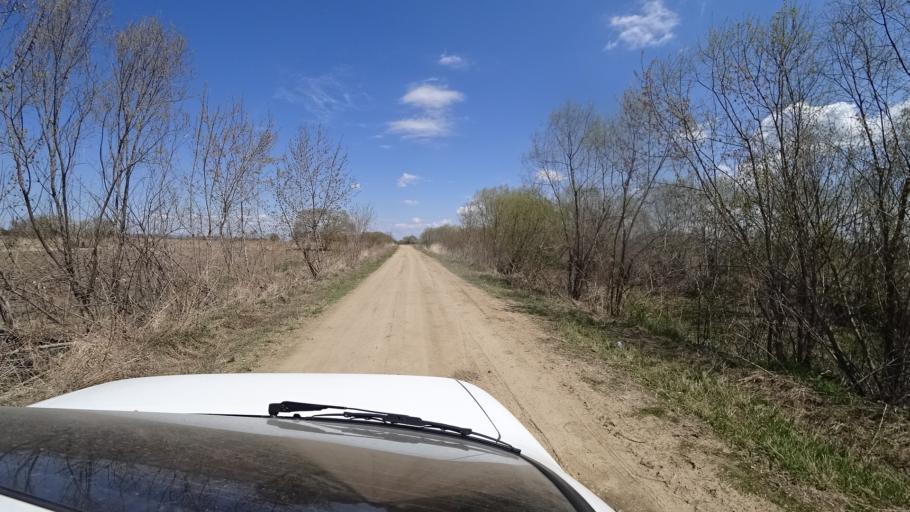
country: RU
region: Primorskiy
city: Dal'nerechensk
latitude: 45.8001
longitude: 133.7697
